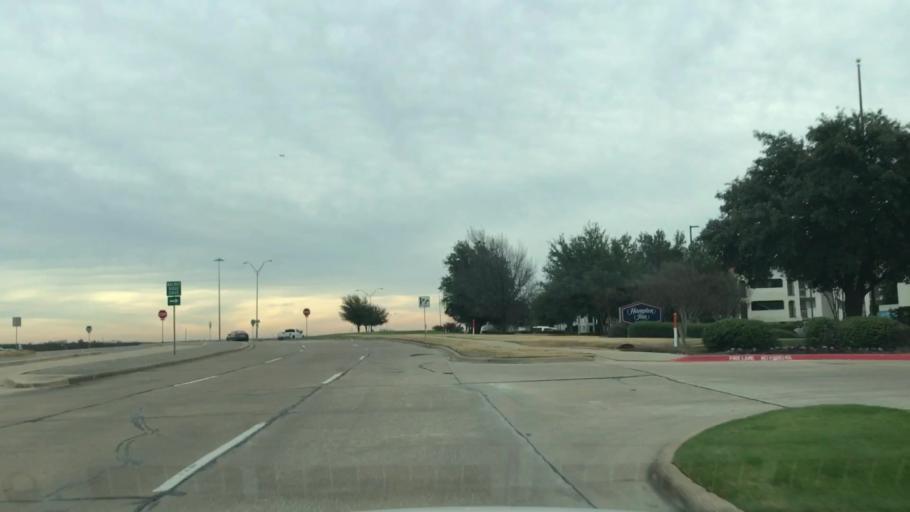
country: US
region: Texas
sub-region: Dallas County
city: Irving
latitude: 32.8849
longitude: -96.9586
